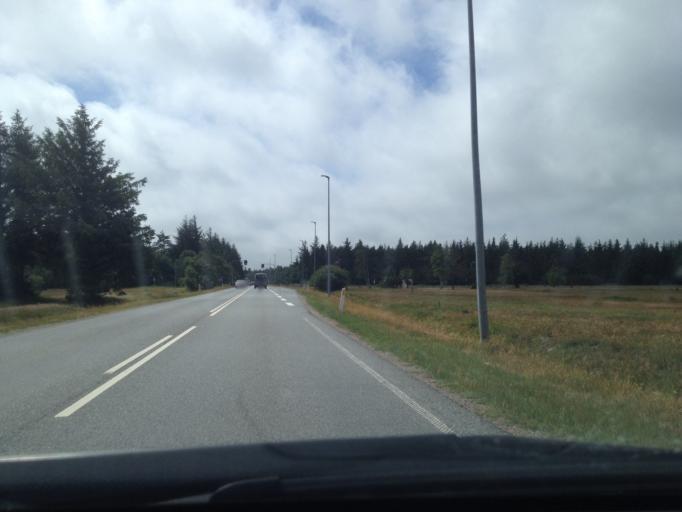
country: DK
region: South Denmark
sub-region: Varde Kommune
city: Oksbol
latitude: 55.6074
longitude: 8.2270
